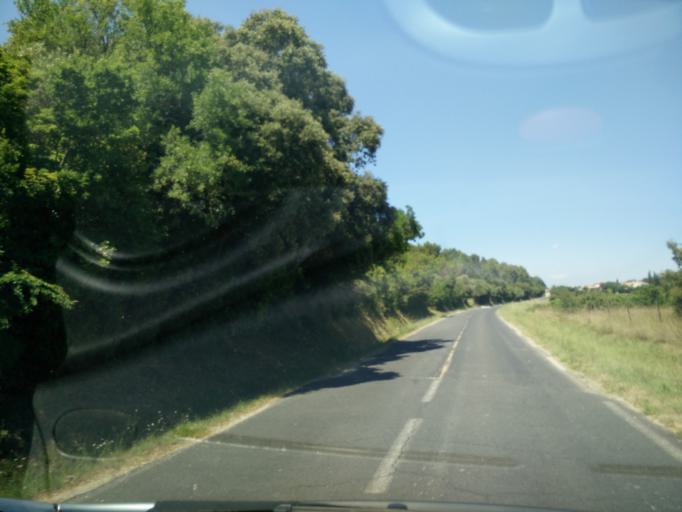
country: FR
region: Languedoc-Roussillon
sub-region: Departement de l'Herault
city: Villetelle
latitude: 43.7162
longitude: 4.1126
